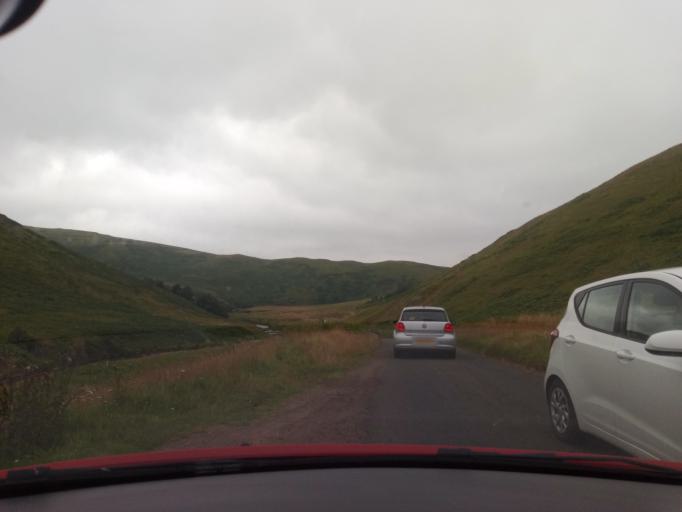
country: GB
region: England
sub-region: Northumberland
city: Rochester
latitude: 55.3609
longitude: -2.1791
